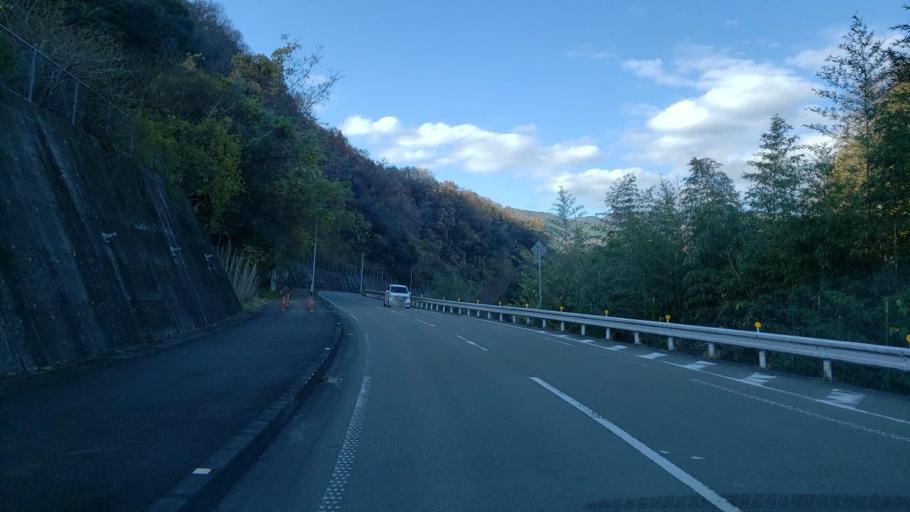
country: JP
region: Tokushima
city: Wakimachi
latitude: 34.0373
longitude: 134.0278
